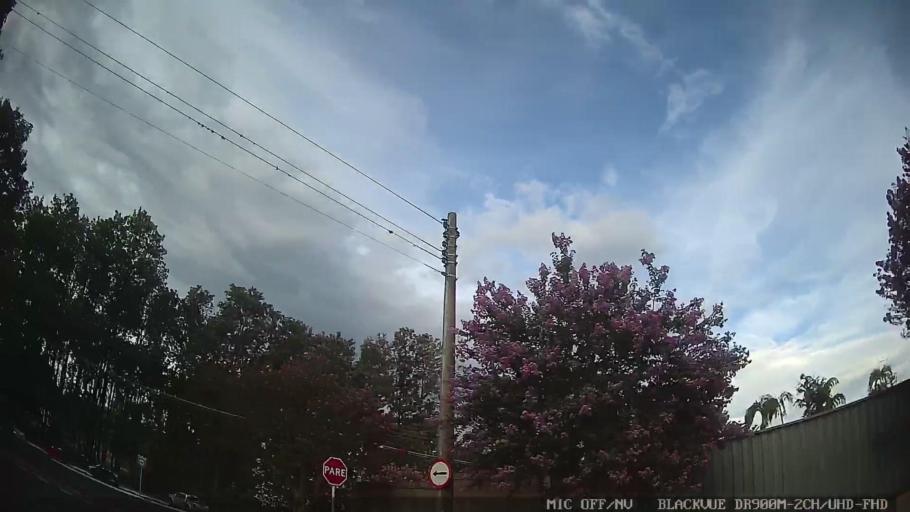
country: BR
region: Sao Paulo
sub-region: Jaguariuna
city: Jaguariuna
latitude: -22.6386
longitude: -47.0513
